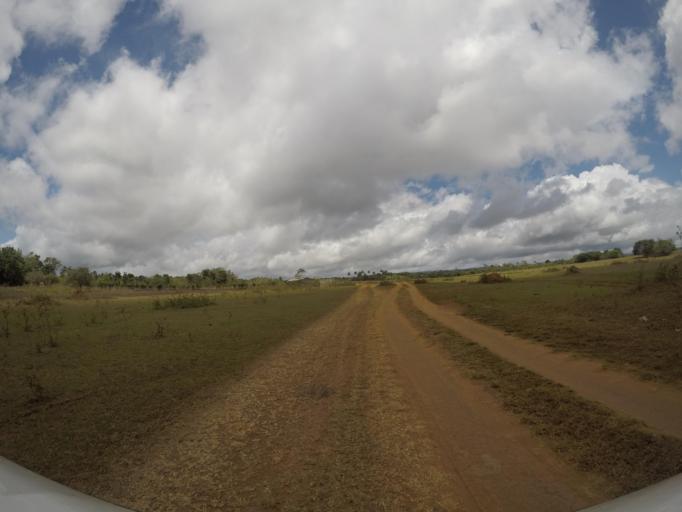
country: TL
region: Lautem
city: Lospalos
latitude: -8.4723
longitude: 126.9879
